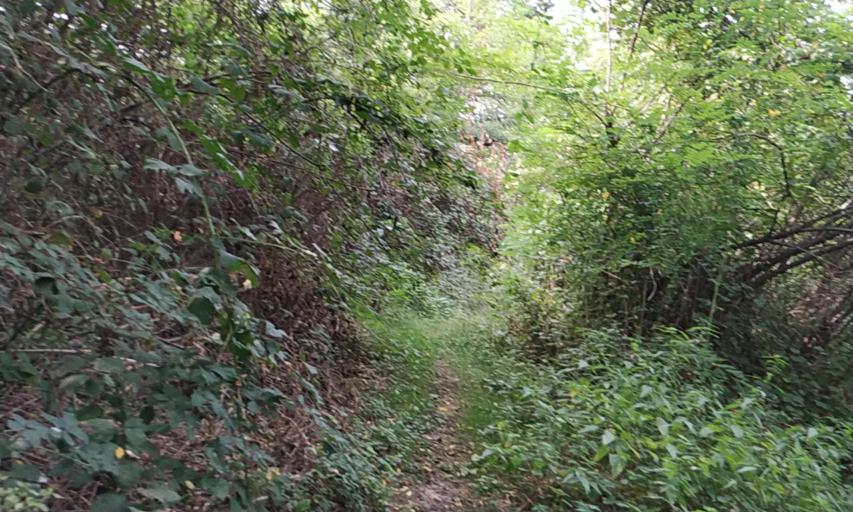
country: IT
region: Piedmont
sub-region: Provincia di Biella
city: Dorzano
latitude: 45.4293
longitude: 8.0922
